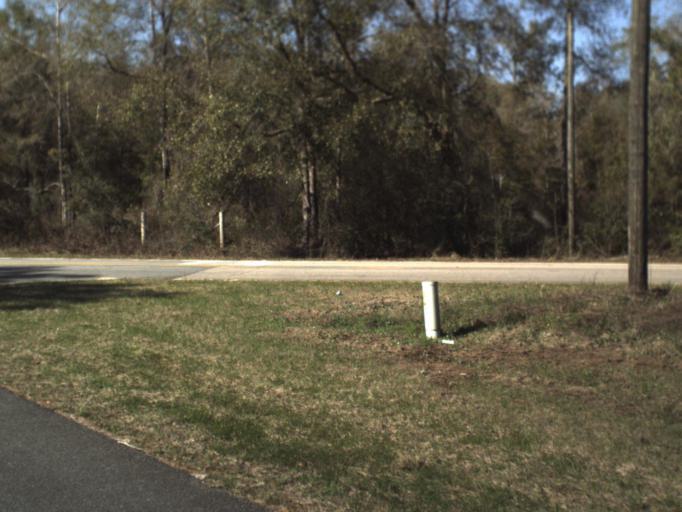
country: US
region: Florida
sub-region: Gulf County
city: Wewahitchka
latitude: 30.2365
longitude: -85.2127
